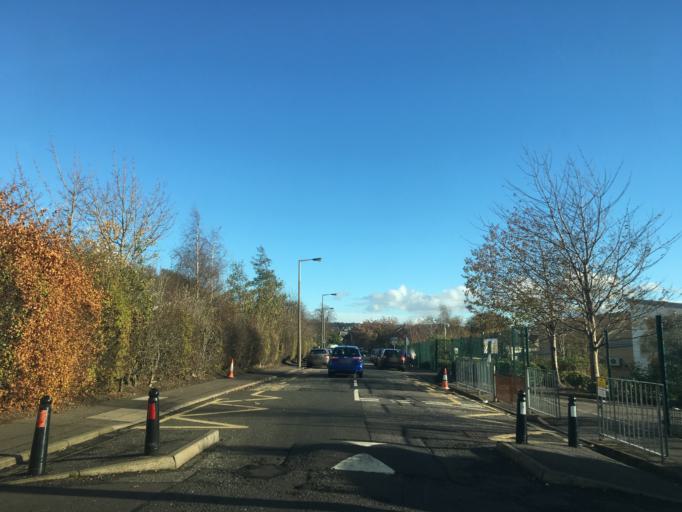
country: GB
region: Scotland
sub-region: Edinburgh
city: Colinton
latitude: 55.9133
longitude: -3.2359
